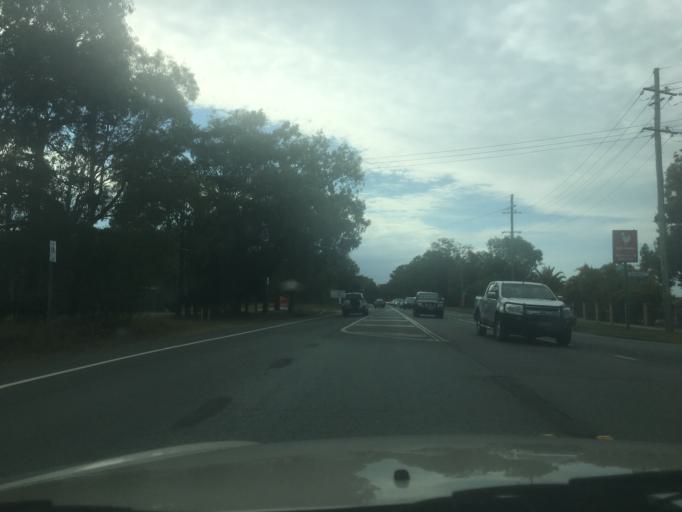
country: AU
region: Queensland
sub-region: Moreton Bay
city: Bongaree
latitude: -27.0695
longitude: 153.1322
